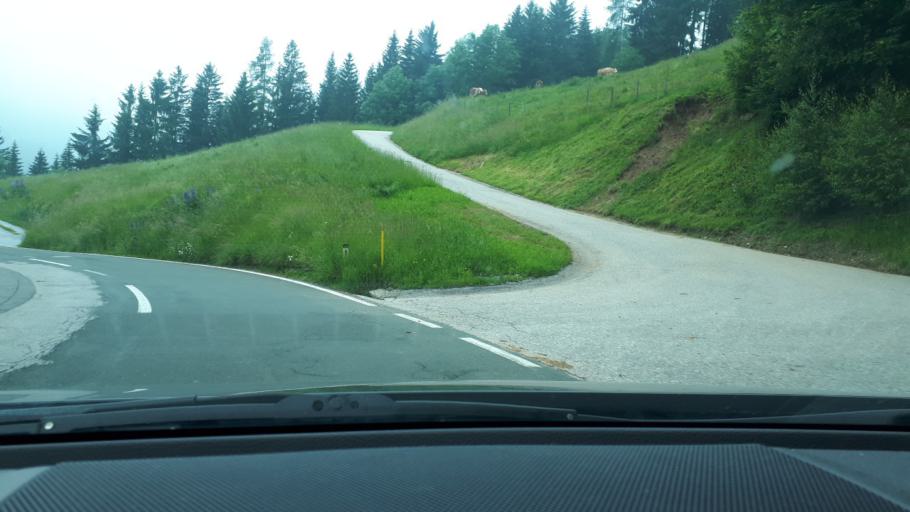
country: AT
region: Carinthia
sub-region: Politischer Bezirk Wolfsberg
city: Preitenegg
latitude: 46.9356
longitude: 14.8994
